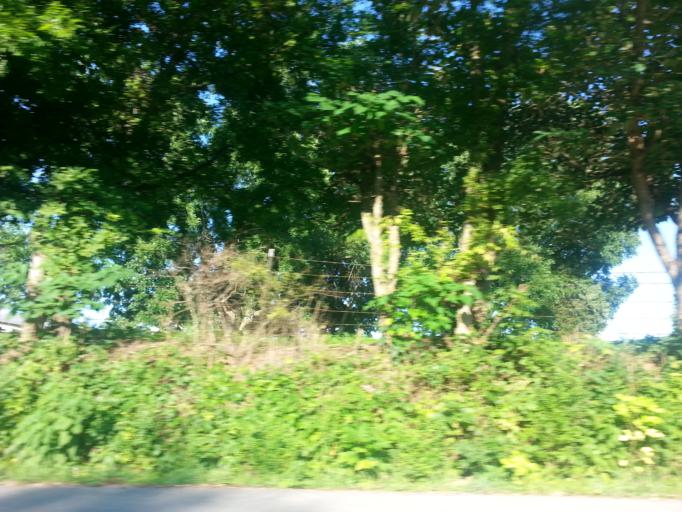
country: US
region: Tennessee
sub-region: Blount County
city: Wildwood
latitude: 35.7536
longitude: -83.8826
